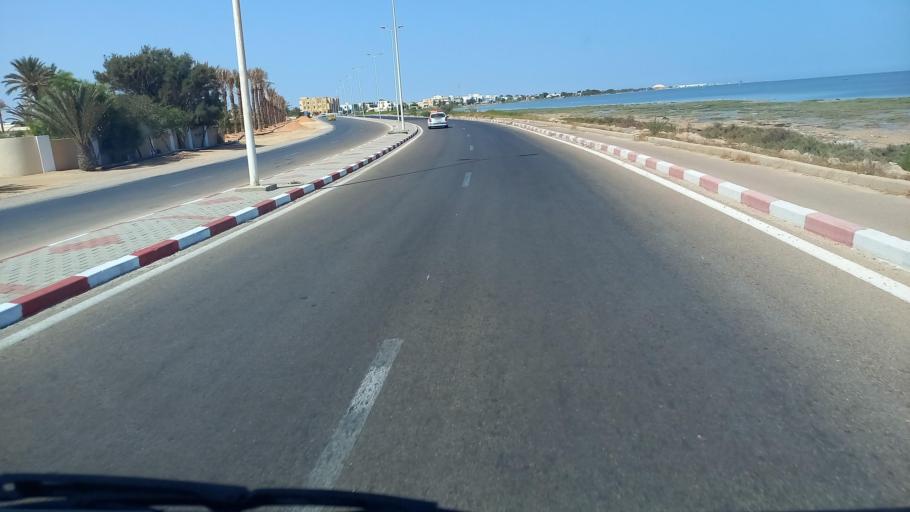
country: TN
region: Madanin
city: Houmt Souk
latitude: 33.8746
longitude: 10.9037
